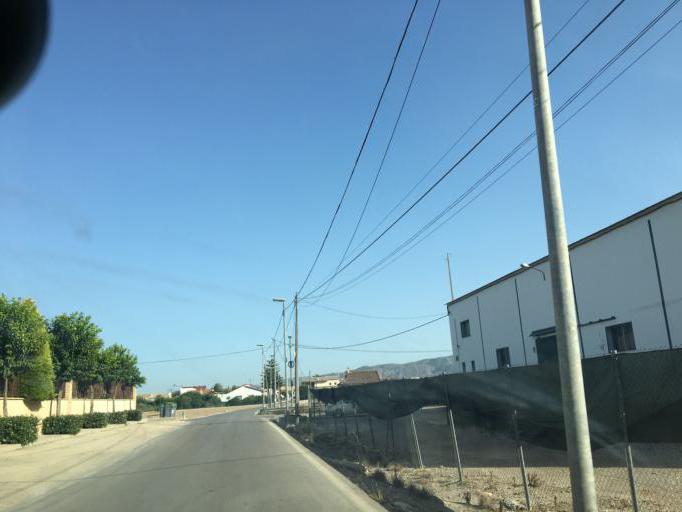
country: ES
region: Murcia
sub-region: Murcia
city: Santomera
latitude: 38.0309
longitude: -1.0683
